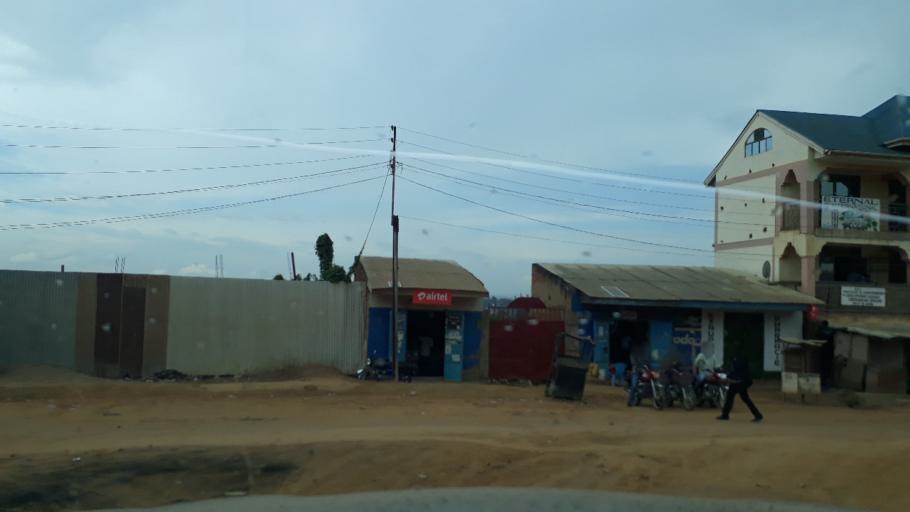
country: CD
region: Eastern Province
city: Bunia
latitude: 1.5630
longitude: 30.2472
